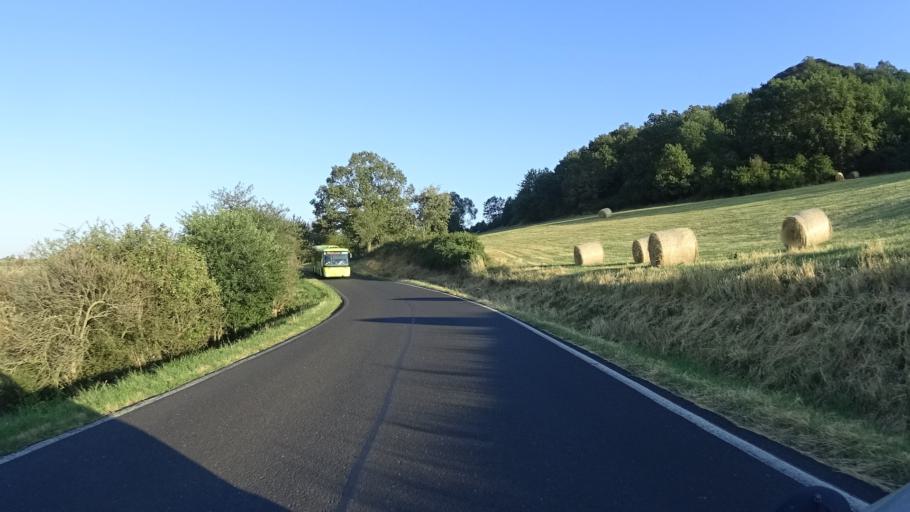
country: CZ
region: Ustecky
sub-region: Okres Litomerice
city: Litomerice
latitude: 50.5624
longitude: 14.1182
